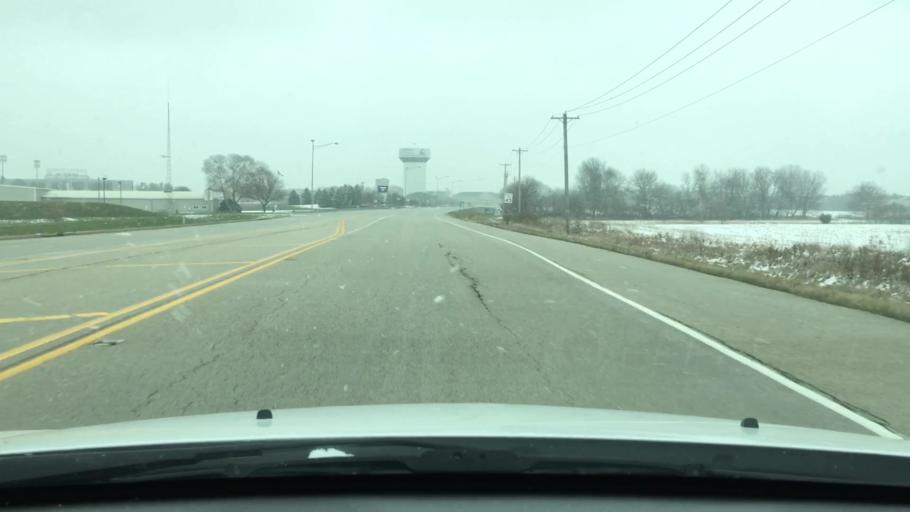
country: US
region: Illinois
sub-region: DeKalb County
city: DeKalb
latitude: 41.9328
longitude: -88.7899
